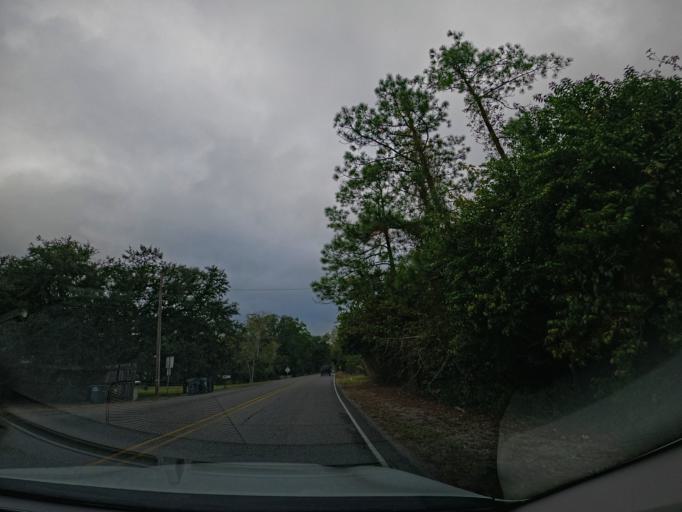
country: US
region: Louisiana
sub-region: Terrebonne Parish
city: Houma
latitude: 29.5739
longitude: -90.7486
